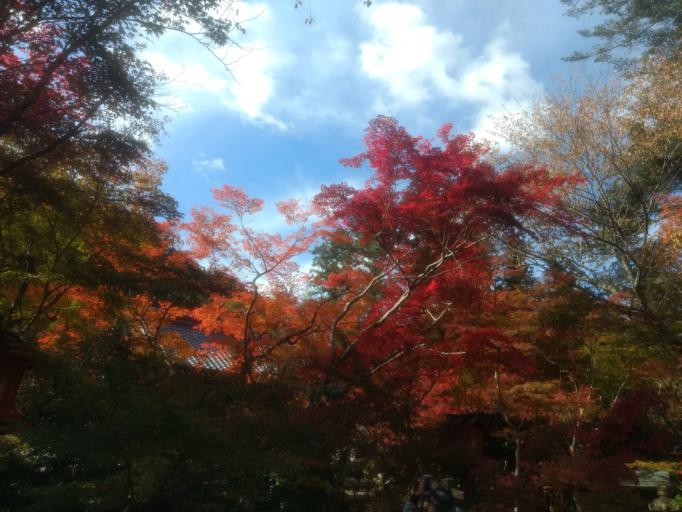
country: JP
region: Kyoto
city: Kameoka
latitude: 35.0009
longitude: 135.5834
